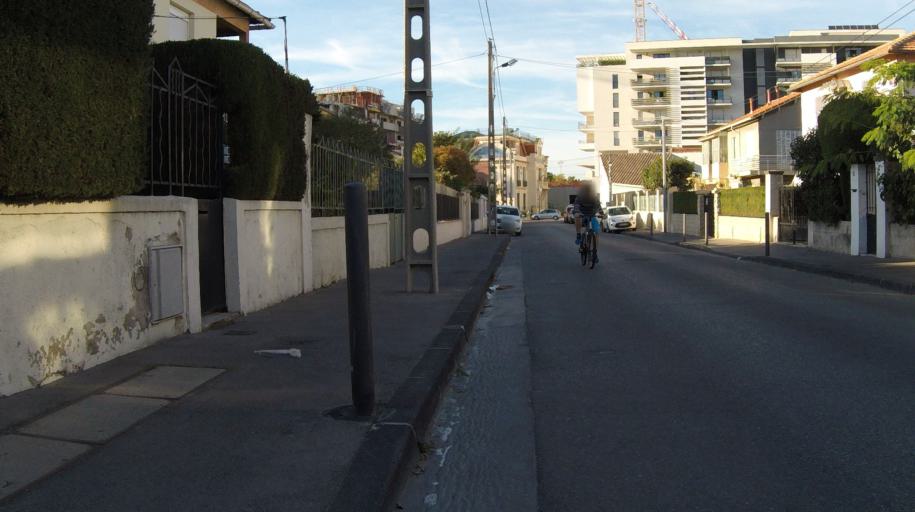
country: FR
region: Provence-Alpes-Cote d'Azur
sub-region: Departement des Bouches-du-Rhone
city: Marseille 10
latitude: 43.2807
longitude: 5.4242
